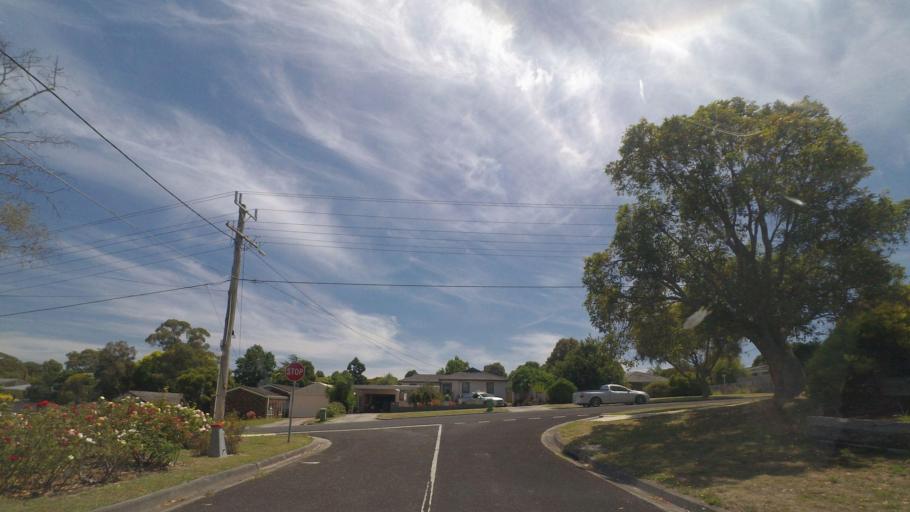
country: AU
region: Victoria
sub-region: Maroondah
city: Croydon North
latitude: -37.7716
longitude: 145.3197
